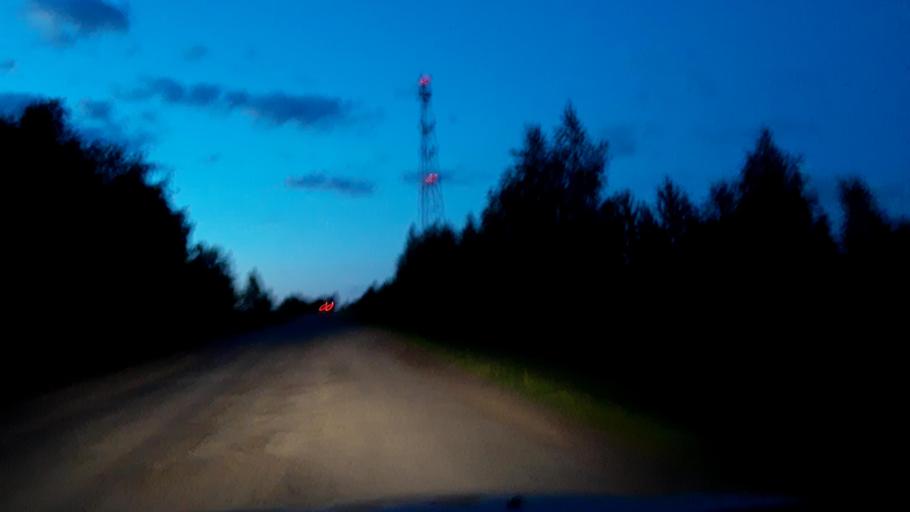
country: RU
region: Nizjnij Novgorod
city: Pamyat' Parizhskoy Kommuny
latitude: 56.0543
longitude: 44.4472
